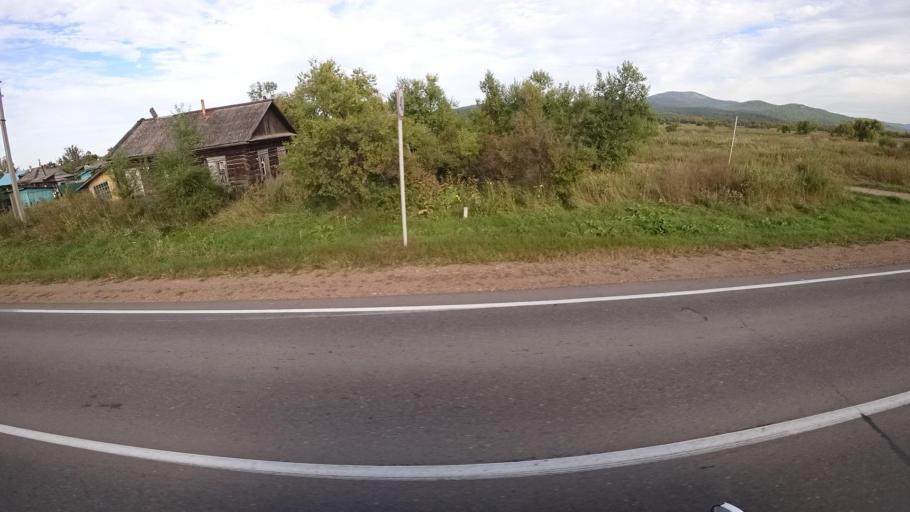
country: RU
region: Primorskiy
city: Dostoyevka
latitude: 44.2852
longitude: 133.4263
